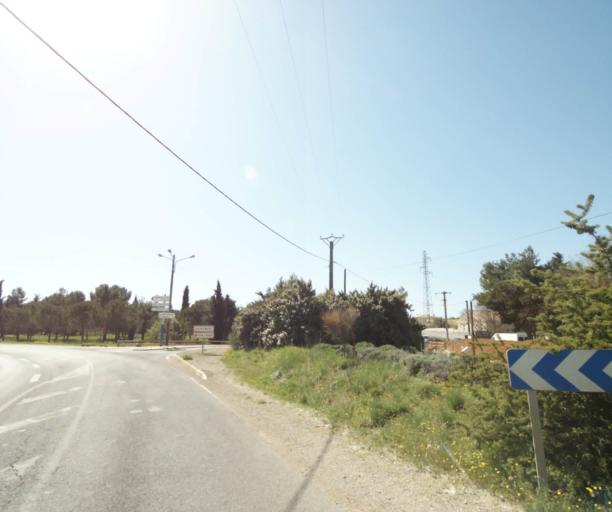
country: FR
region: Languedoc-Roussillon
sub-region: Departement de l'Herault
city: Saint-Bres
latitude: 43.6730
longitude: 4.0261
